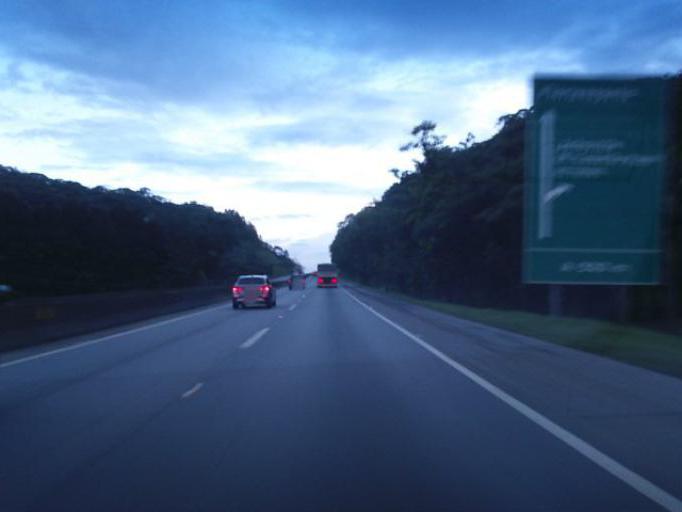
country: BR
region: Santa Catarina
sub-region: Joinville
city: Joinville
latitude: -26.2222
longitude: -48.9164
